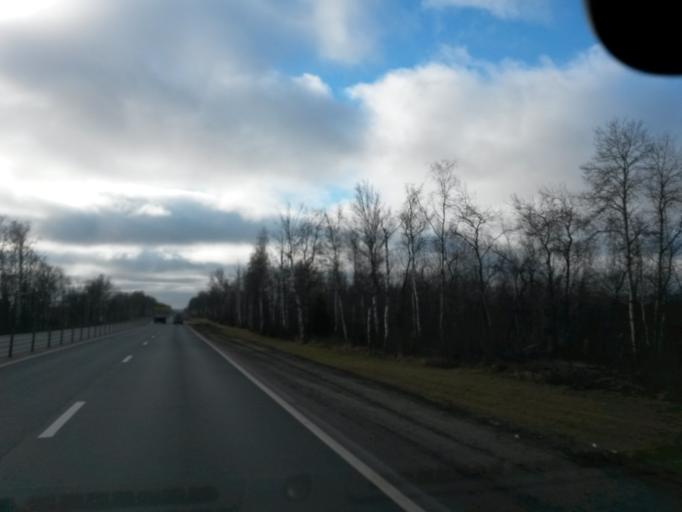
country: RU
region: Jaroslavl
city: Semibratovo
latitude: 57.3376
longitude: 39.5792
